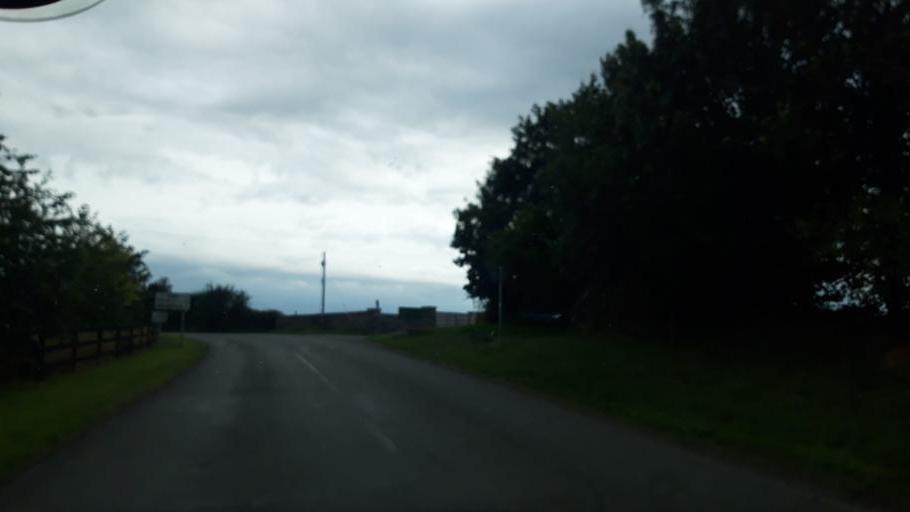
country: IE
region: Leinster
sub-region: Kilkenny
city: Ballyragget
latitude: 52.7859
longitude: -7.3426
